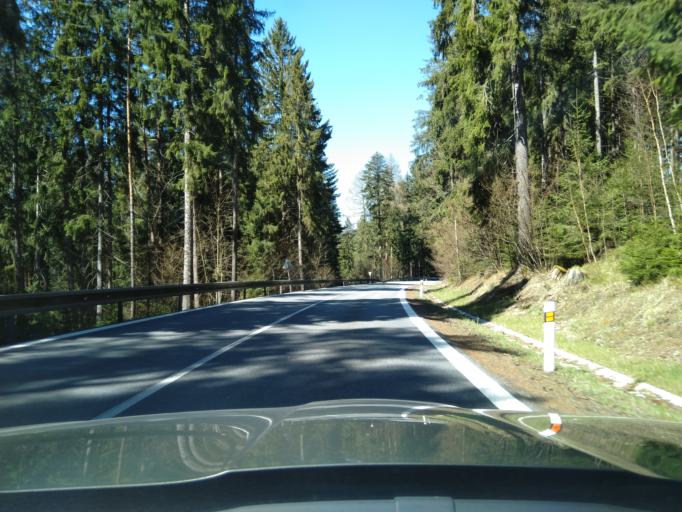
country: CZ
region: Jihocesky
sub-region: Okres Prachatice
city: Vimperk
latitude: 49.0394
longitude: 13.7619
